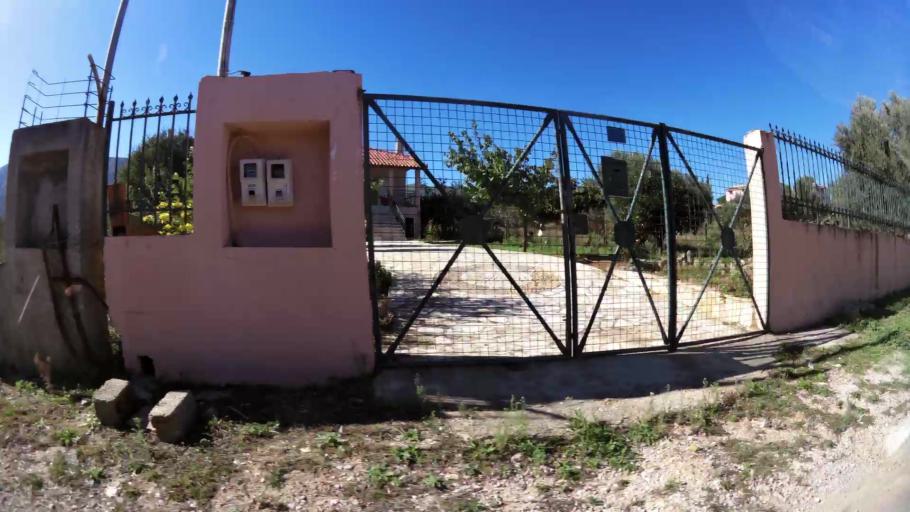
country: GR
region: Attica
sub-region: Nomarchia Anatolikis Attikis
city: Paiania
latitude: 37.9689
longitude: 23.8611
